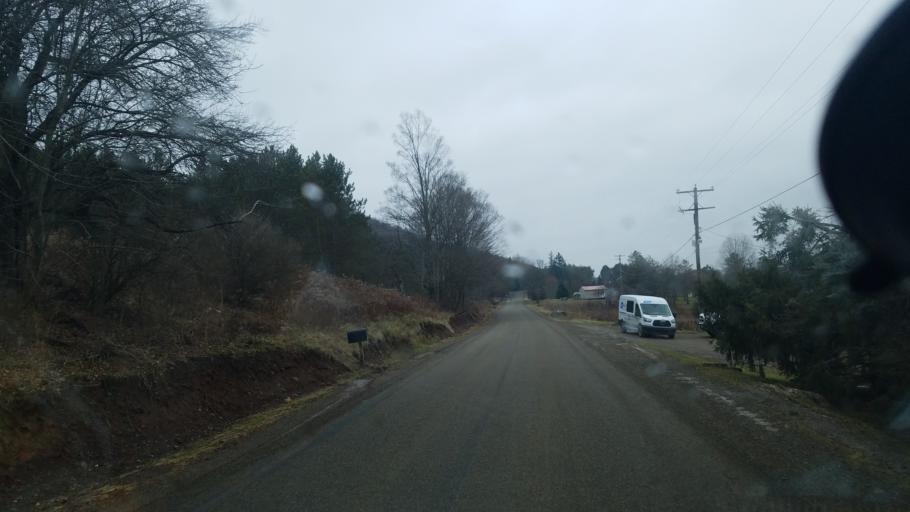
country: US
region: New York
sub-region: Allegany County
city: Wellsville
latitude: 41.9606
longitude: -77.8418
